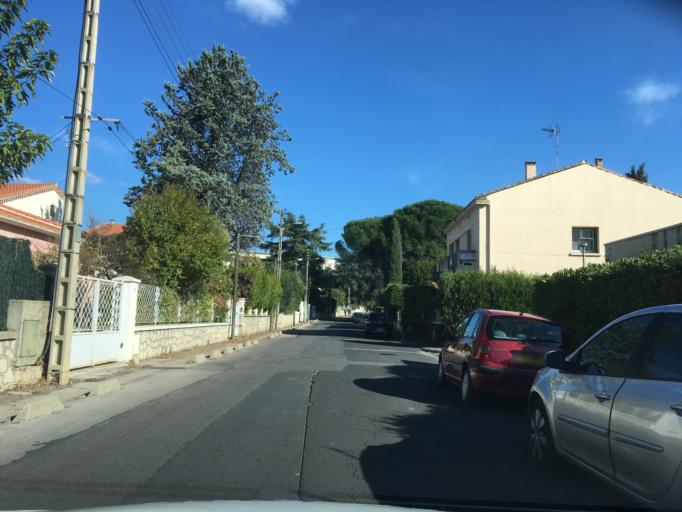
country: FR
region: Languedoc-Roussillon
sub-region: Departement de l'Herault
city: Juvignac
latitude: 43.6116
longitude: 3.8357
